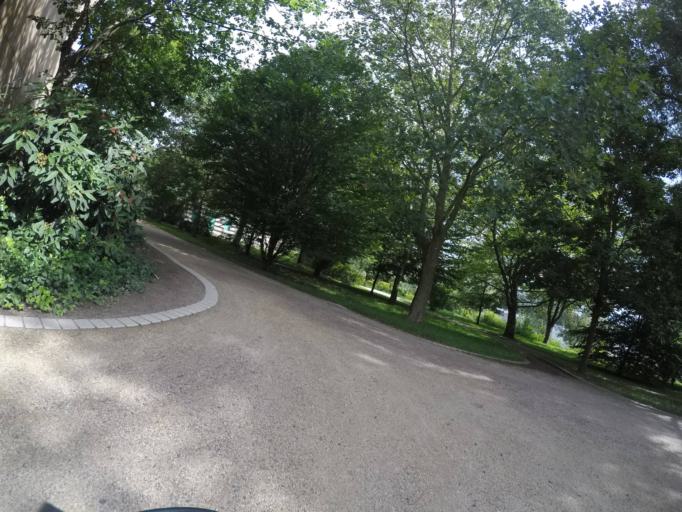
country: DE
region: Brandenburg
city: Potsdam
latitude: 52.3958
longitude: 13.0439
